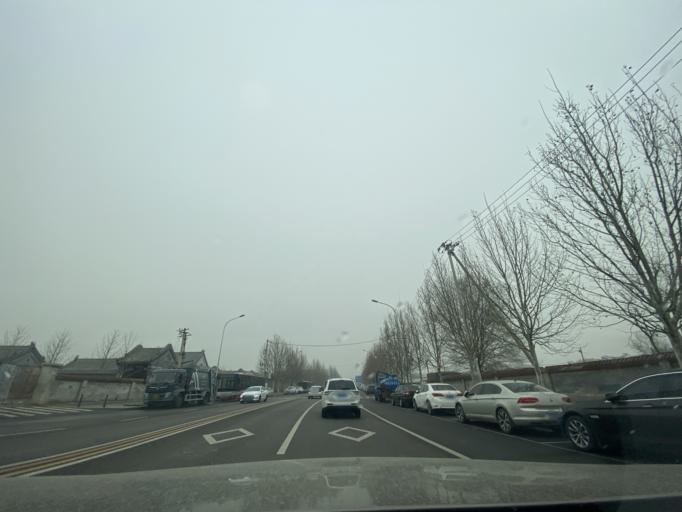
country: CN
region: Beijing
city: Sijiqing
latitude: 39.9684
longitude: 116.2405
